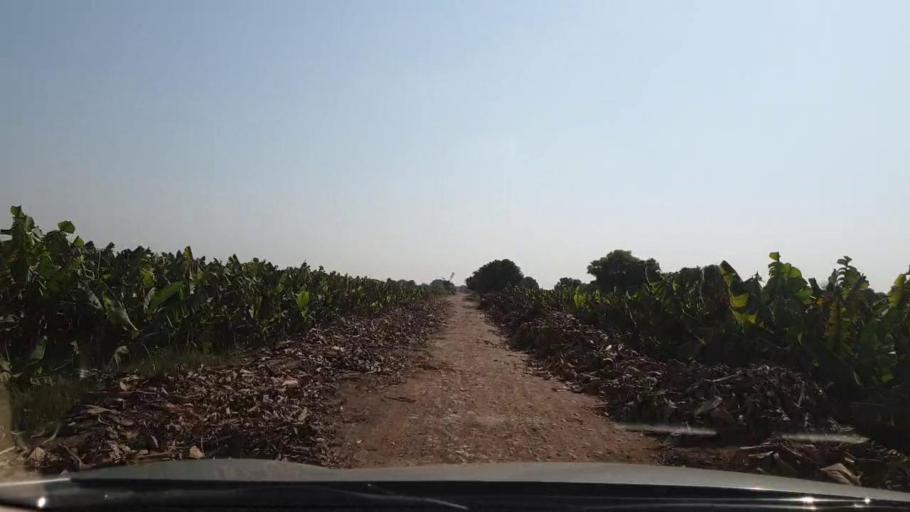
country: PK
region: Sindh
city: Mirpur Khas
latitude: 25.5998
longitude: 68.8673
